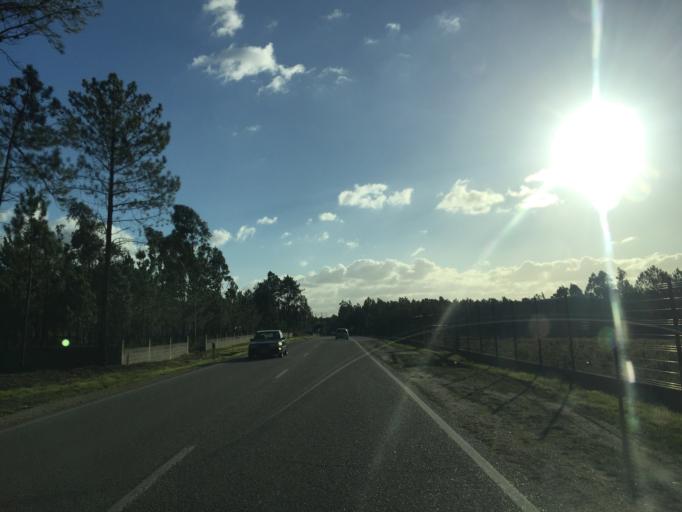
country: PT
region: Leiria
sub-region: Leiria
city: Monte Redondo
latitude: 39.9244
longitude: -8.8080
